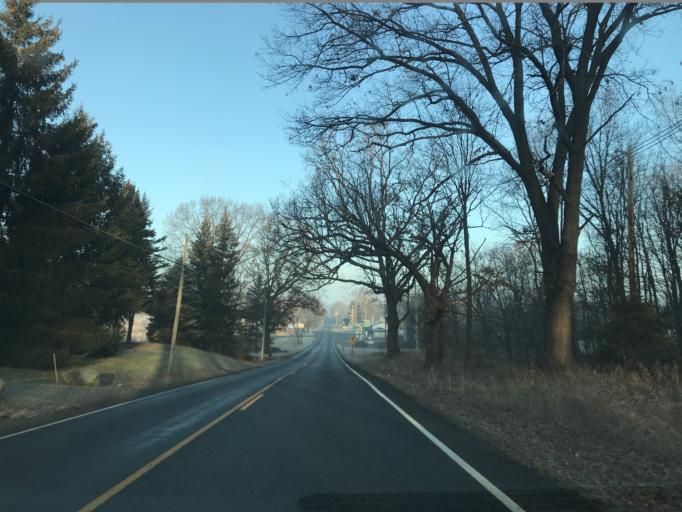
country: US
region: Michigan
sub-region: Ingham County
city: Leslie
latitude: 42.3839
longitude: -84.4531
